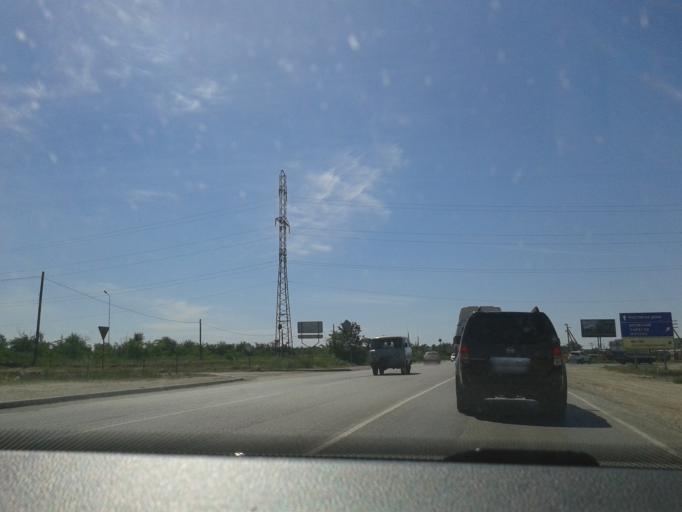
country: RU
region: Volgograd
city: Volgograd
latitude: 48.7044
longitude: 44.4440
